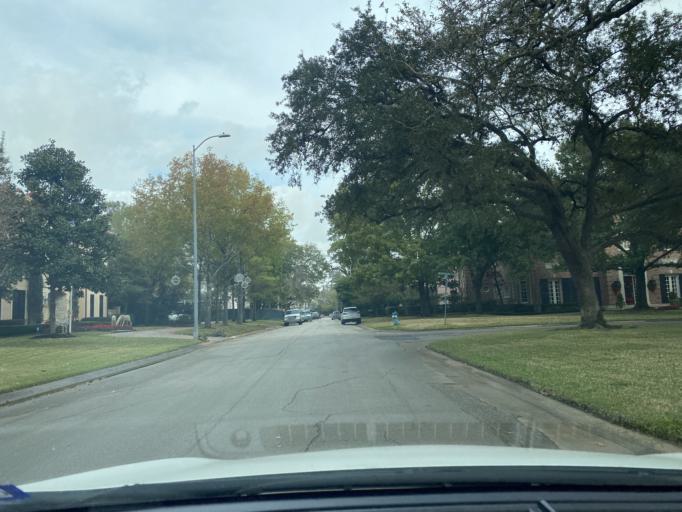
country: US
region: Texas
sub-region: Harris County
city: Hunters Creek Village
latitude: 29.7661
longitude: -95.4709
